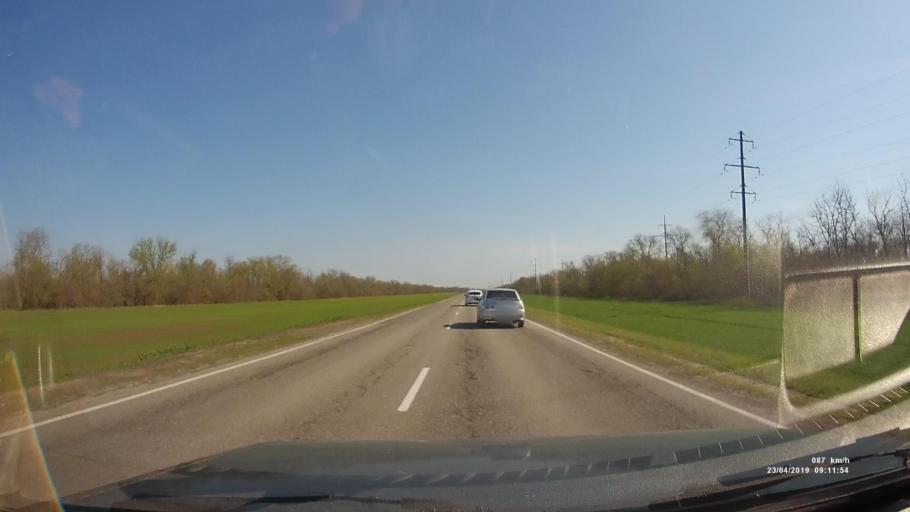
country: RU
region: Rostov
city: Proletarsk
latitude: 46.6001
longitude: 41.6327
